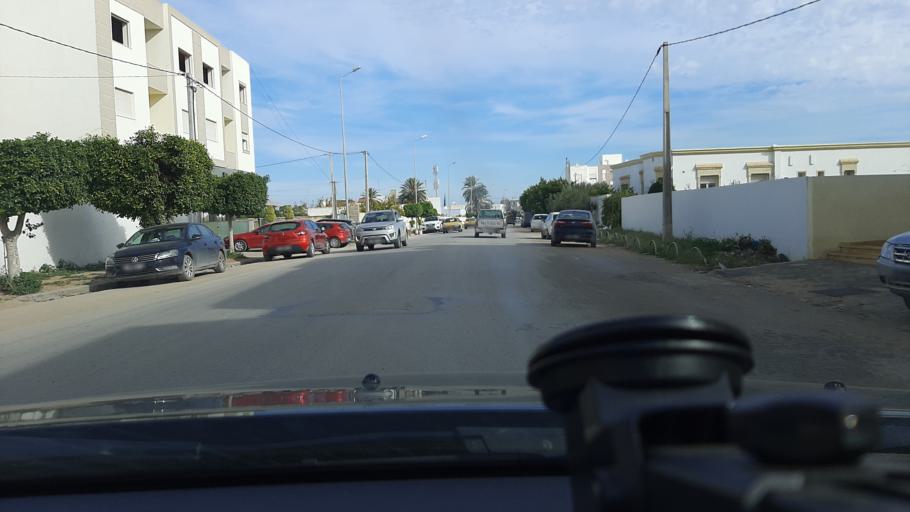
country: TN
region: Safaqis
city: Sfax
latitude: 34.7648
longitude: 10.7293
